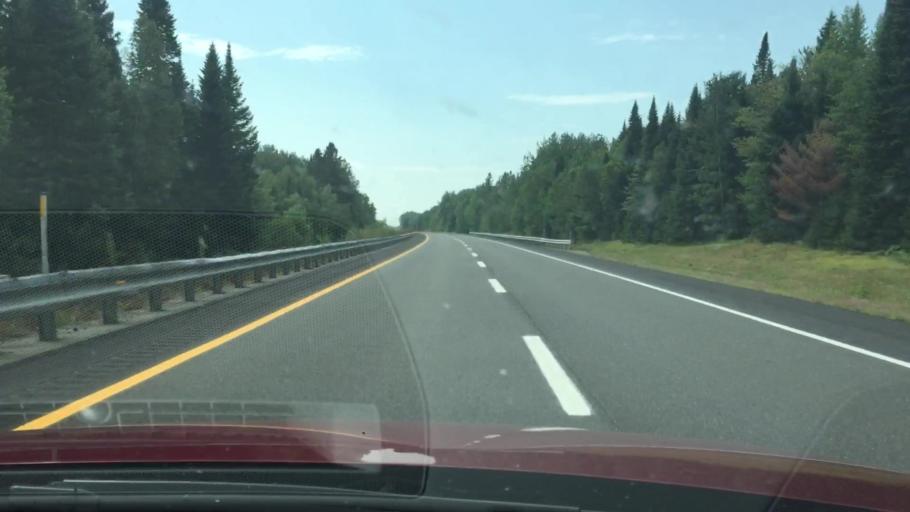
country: US
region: Maine
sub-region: Penobscot County
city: Patten
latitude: 46.0428
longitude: -68.2613
